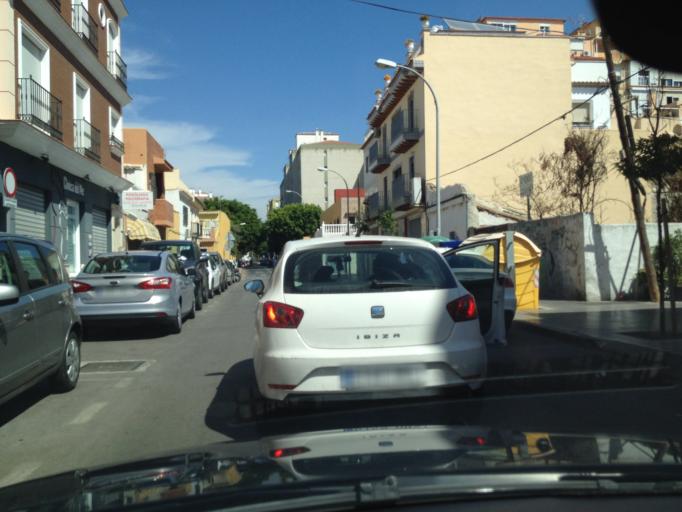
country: ES
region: Andalusia
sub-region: Provincia de Malaga
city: Malaga
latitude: 36.7023
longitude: -4.4363
